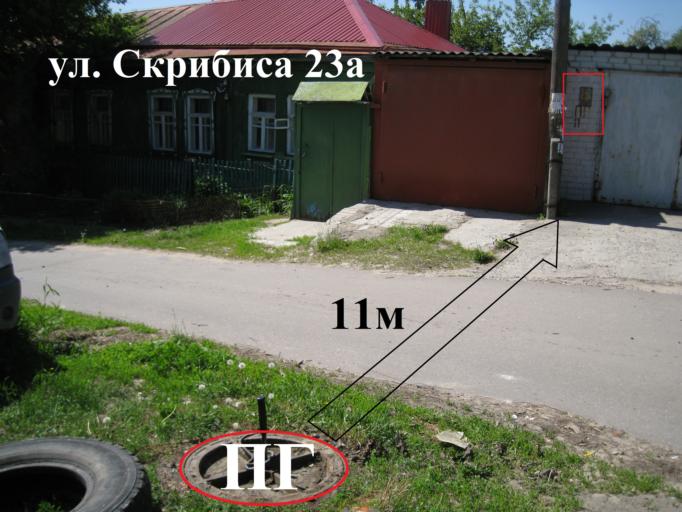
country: RU
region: Voronezj
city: Voronezh
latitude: 51.6377
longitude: 39.2046
